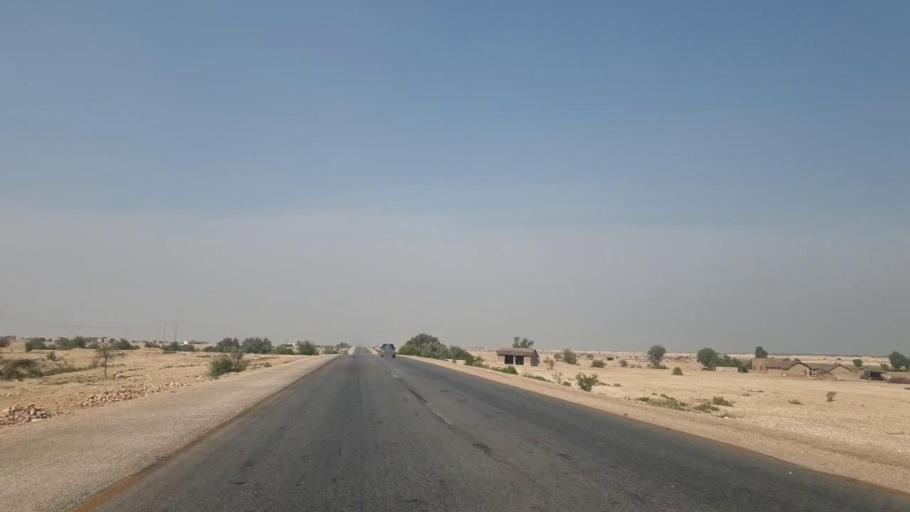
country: PK
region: Sindh
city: Hala
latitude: 25.8380
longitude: 68.2667
